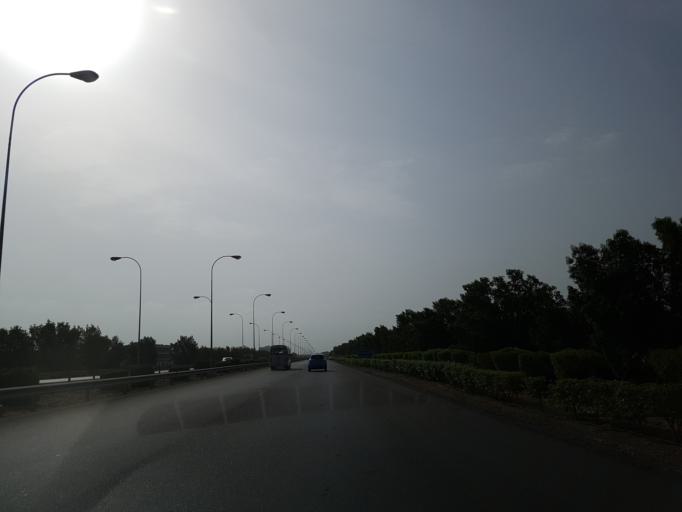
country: OM
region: Al Batinah
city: Al Sohar
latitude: 24.4024
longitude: 56.6600
